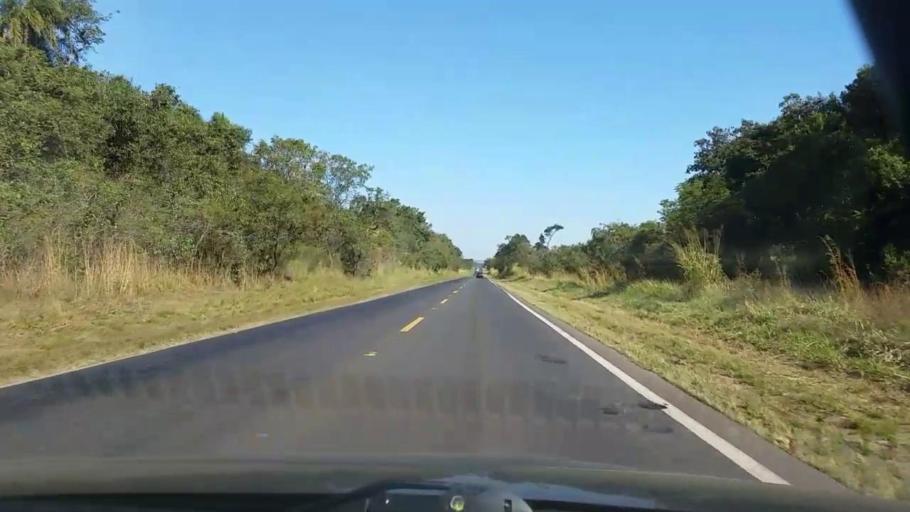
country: BR
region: Sao Paulo
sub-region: Sao Manuel
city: Sao Manuel
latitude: -22.8951
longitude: -48.7634
